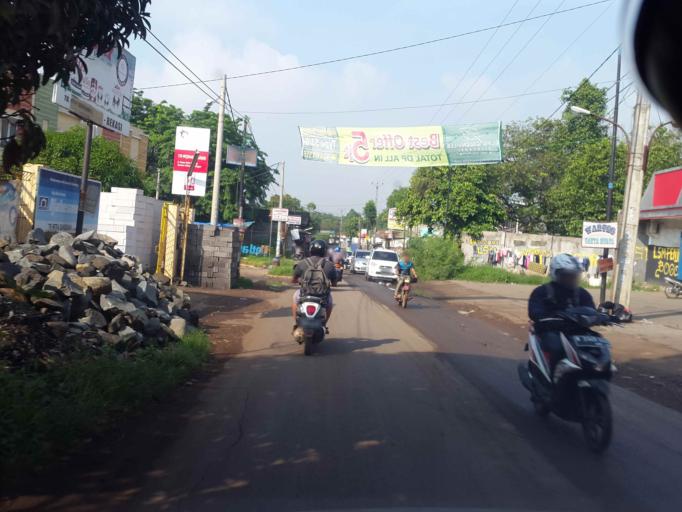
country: ID
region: West Java
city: Cileungsir
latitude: -6.3778
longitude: 106.9968
